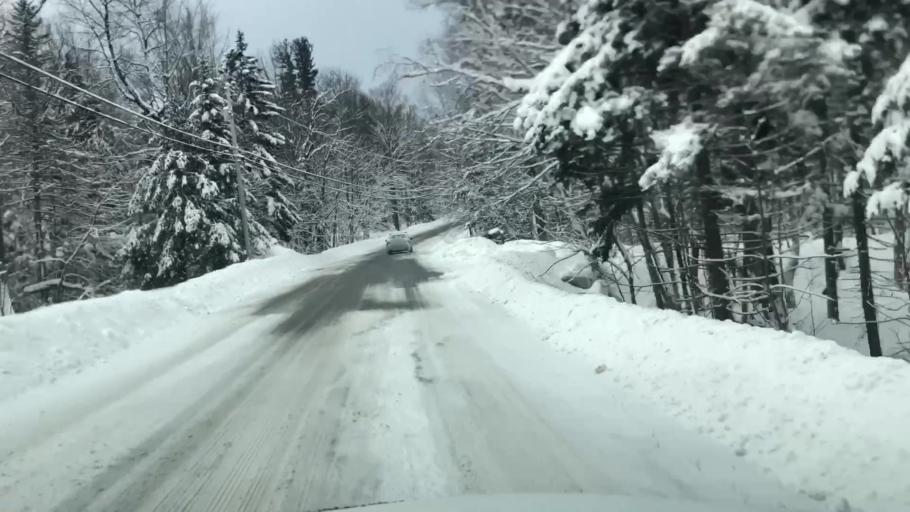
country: US
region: Vermont
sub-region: Rutland County
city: Rutland
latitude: 43.6503
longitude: -72.7825
